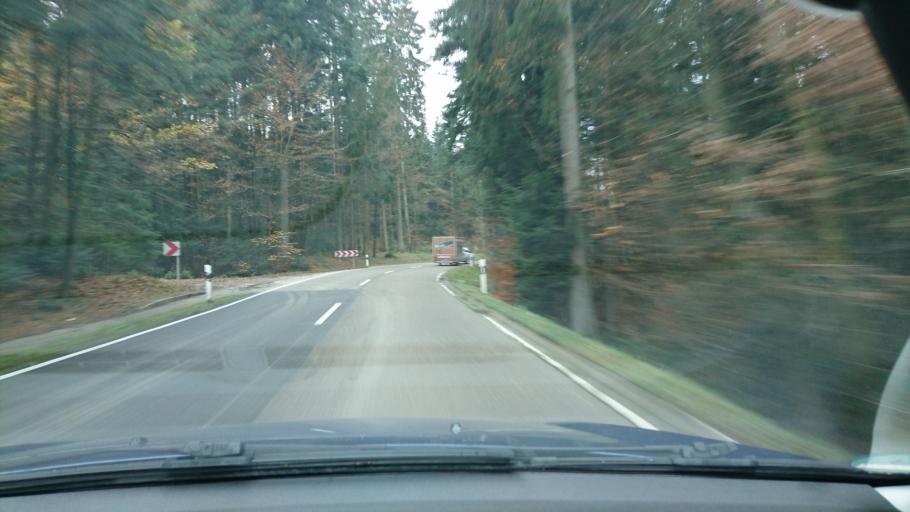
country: DE
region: Baden-Wuerttemberg
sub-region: Regierungsbezirk Stuttgart
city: Welzheim
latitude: 48.8996
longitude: 9.6684
